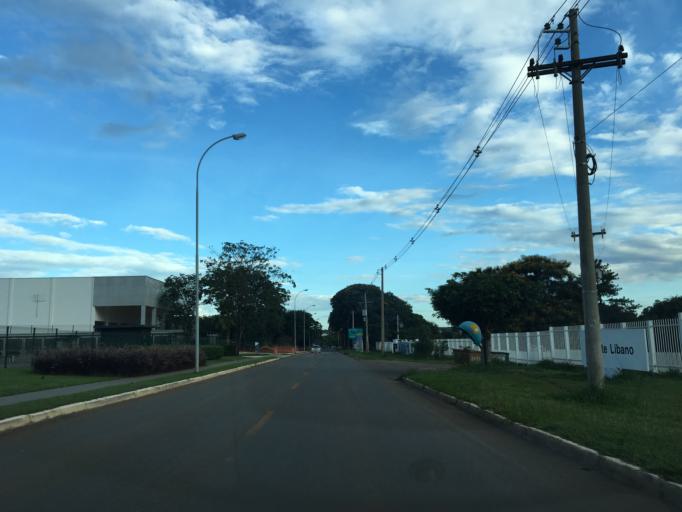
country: BR
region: Federal District
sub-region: Brasilia
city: Brasilia
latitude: -15.8175
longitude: -47.8461
